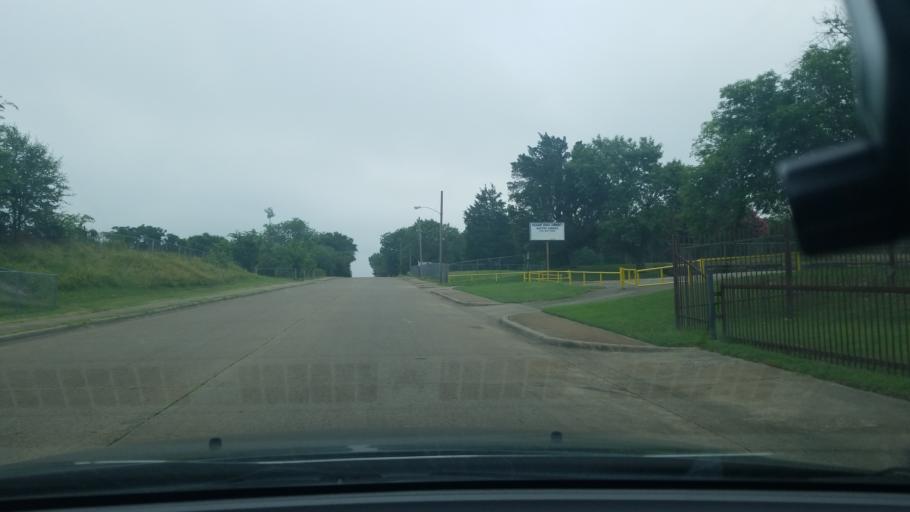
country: US
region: Texas
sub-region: Dallas County
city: Balch Springs
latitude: 32.7593
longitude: -96.6868
